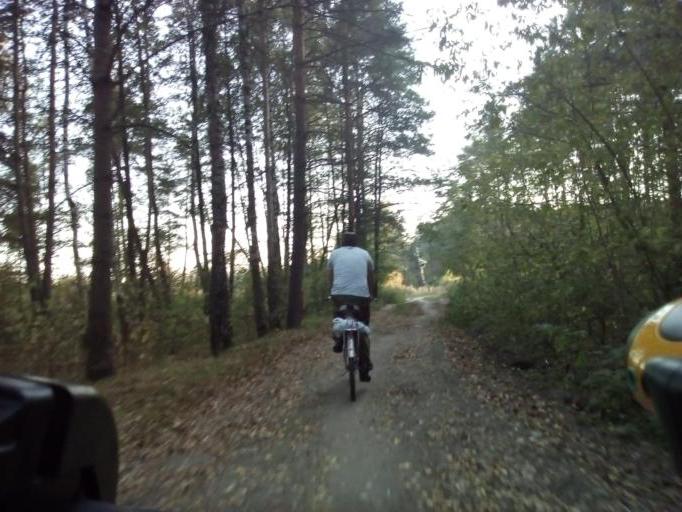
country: RU
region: Moskovskaya
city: Ramenskoye
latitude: 55.5886
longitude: 38.2345
